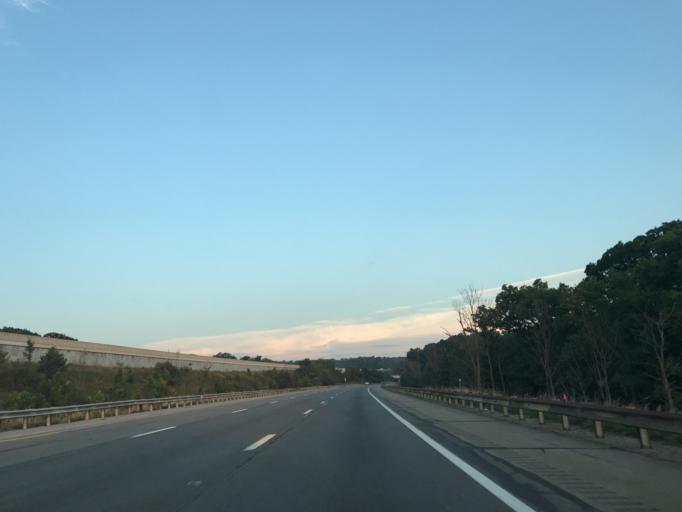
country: US
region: Ohio
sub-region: Summit County
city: Peninsula
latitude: 41.2525
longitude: -81.5765
